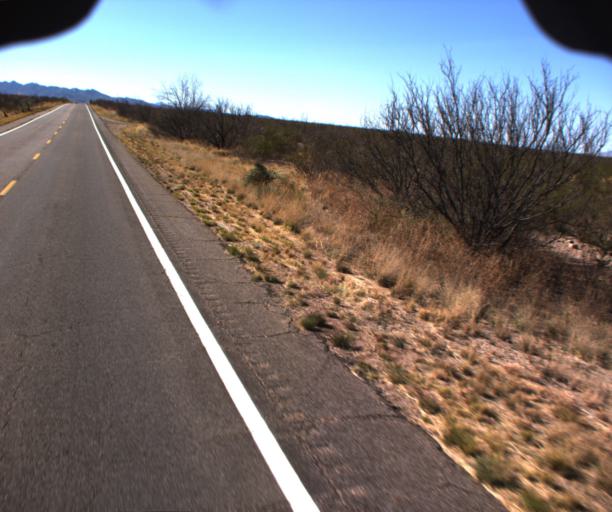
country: US
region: Arizona
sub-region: Cochise County
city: Tombstone
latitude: 31.6091
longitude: -110.0501
